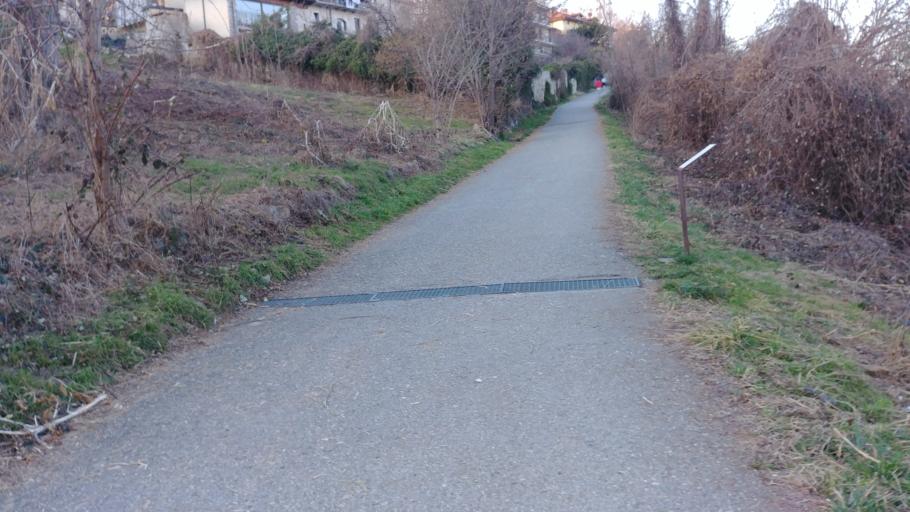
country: IT
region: Piedmont
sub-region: Provincia di Cuneo
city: Cuneo
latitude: 44.3662
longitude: 7.5382
